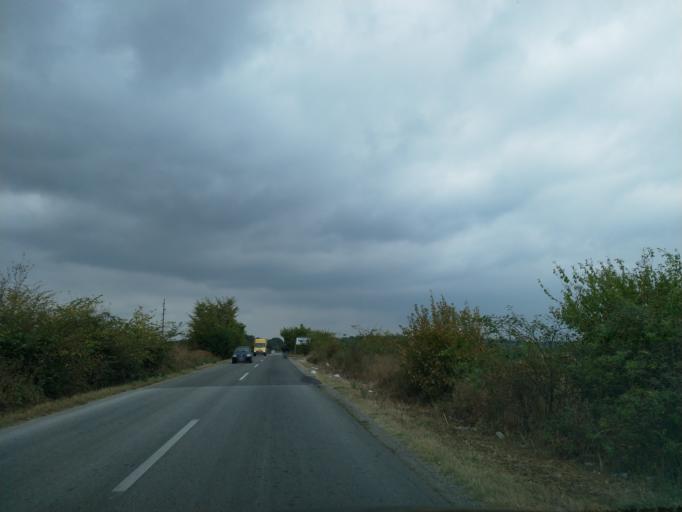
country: RS
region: Central Serbia
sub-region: Pomoravski Okrug
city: Jagodina
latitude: 43.9998
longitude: 21.2152
